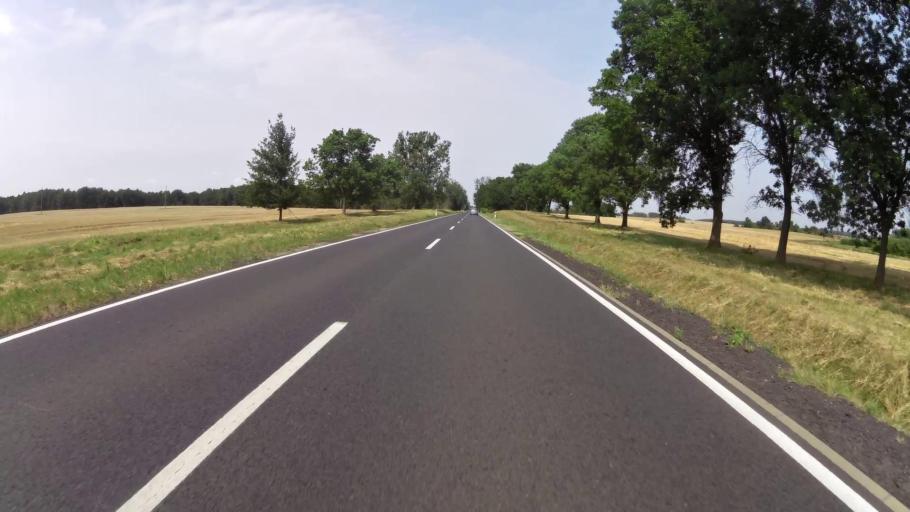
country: PL
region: West Pomeranian Voivodeship
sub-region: Powiat gryfinski
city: Mieszkowice
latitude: 52.8299
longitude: 14.4947
